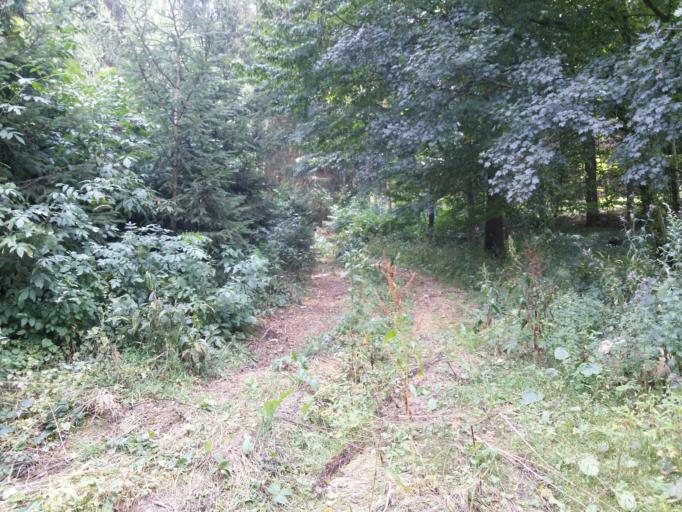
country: CZ
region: South Moravian
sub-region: Okres Znojmo
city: Jevisovice
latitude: 49.0334
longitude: 15.9989
